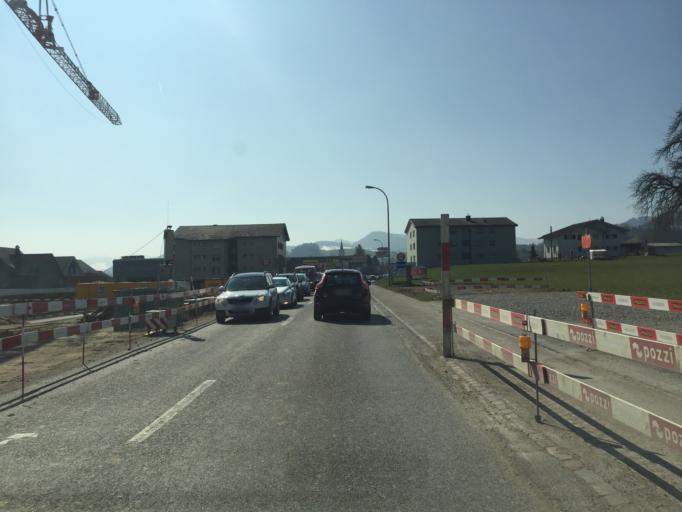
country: CH
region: Saint Gallen
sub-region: Wahlkreis Toggenburg
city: Buetschwil
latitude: 47.3682
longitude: 9.0761
